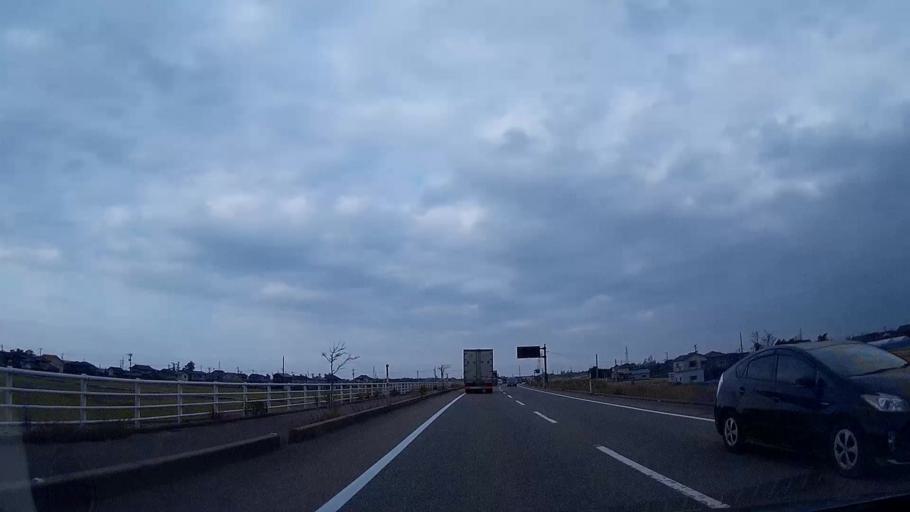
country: JP
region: Toyama
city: Nyuzen
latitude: 36.8956
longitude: 137.4445
